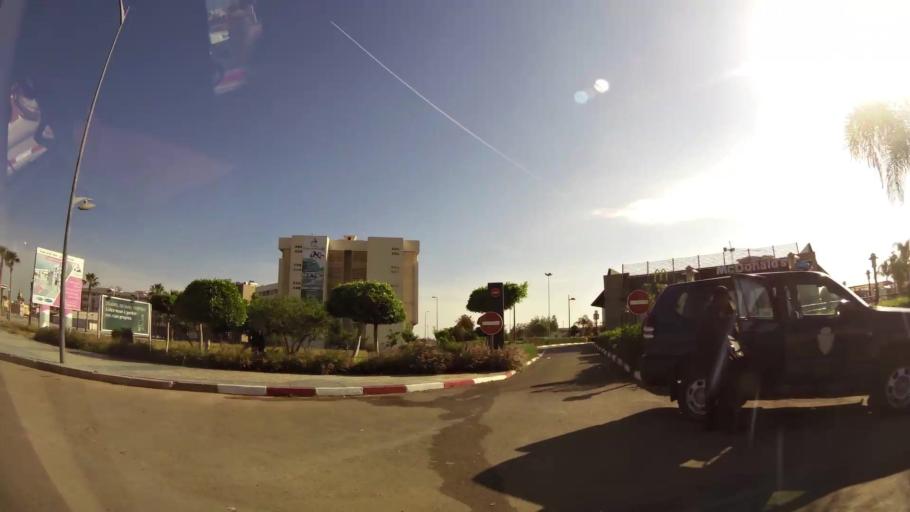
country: MA
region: Oriental
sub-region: Oujda-Angad
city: Oujda
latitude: 34.6768
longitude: -1.9284
